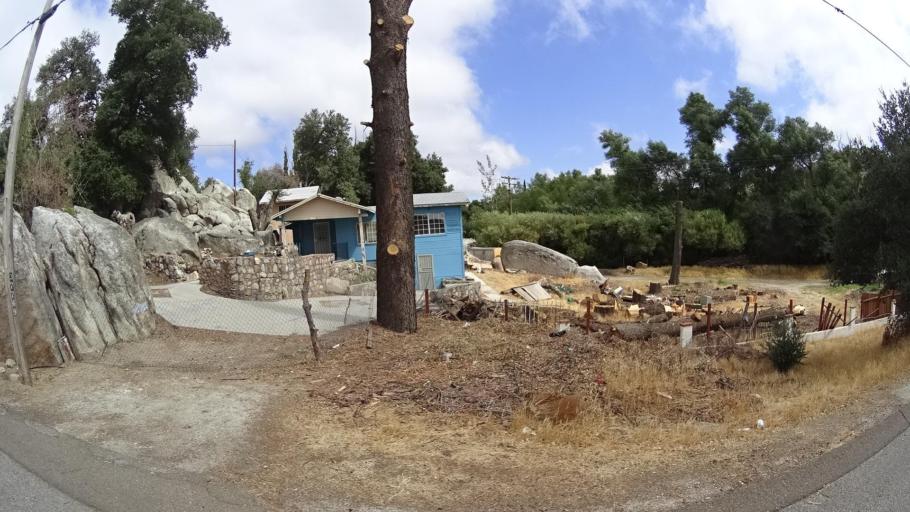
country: US
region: California
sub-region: San Diego County
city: Campo
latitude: 32.6878
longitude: -116.3370
